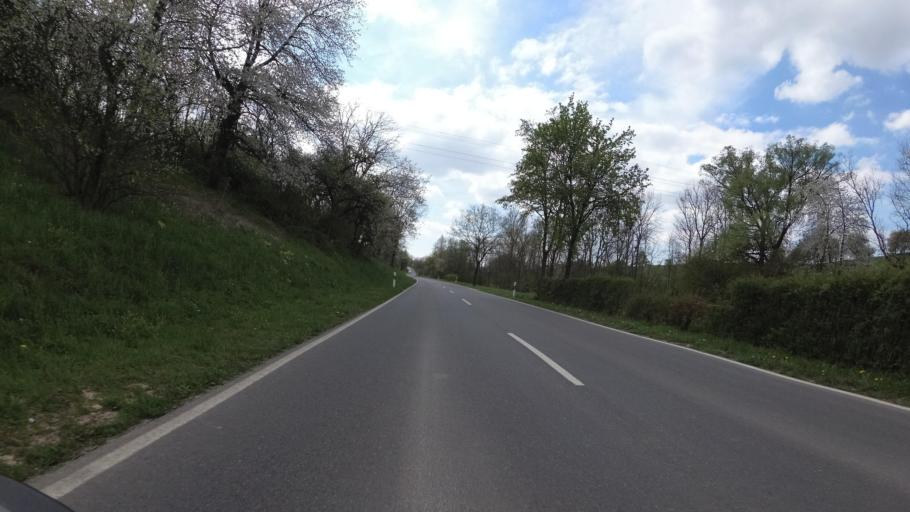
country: DE
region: Baden-Wuerttemberg
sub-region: Regierungsbezirk Stuttgart
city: Widdern
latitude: 49.2556
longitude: 9.4028
